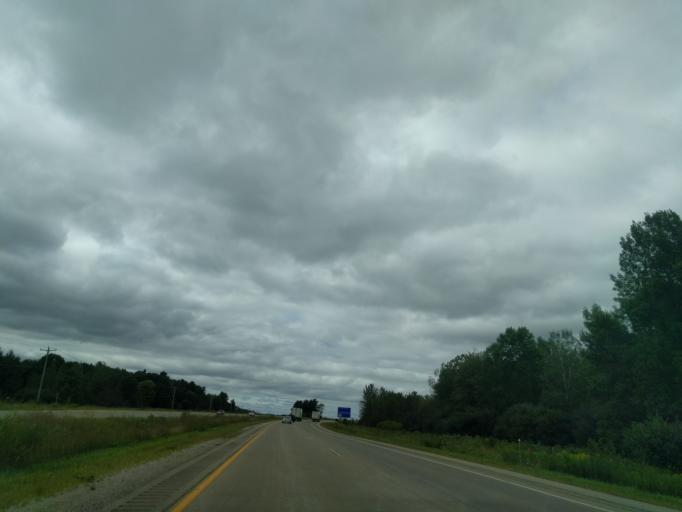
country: US
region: Wisconsin
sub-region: Marinette County
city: Peshtigo
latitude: 45.0633
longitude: -87.6999
